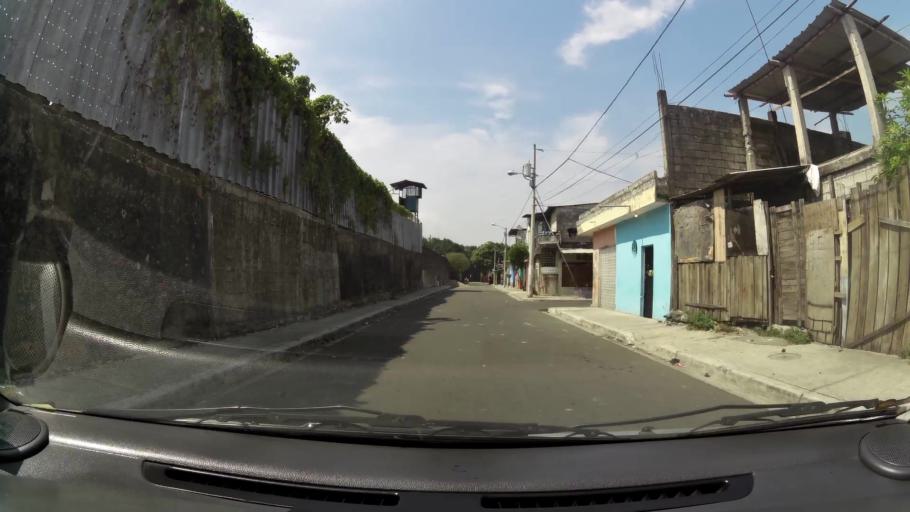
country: EC
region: Guayas
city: Guayaquil
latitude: -2.2663
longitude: -79.8722
